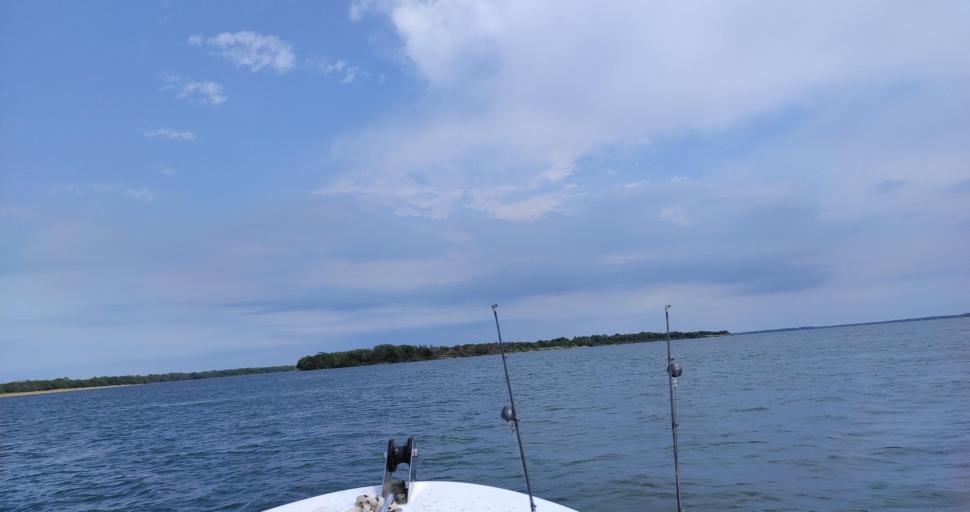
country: PY
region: Neembucu
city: Cerrito
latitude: -27.3617
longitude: -57.6681
